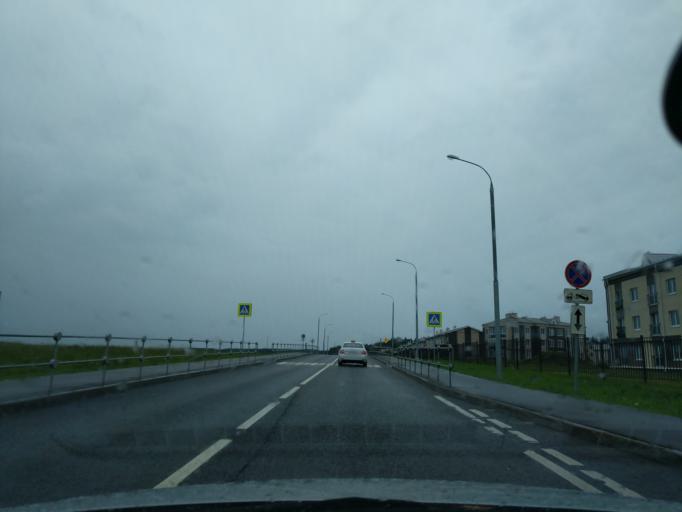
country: RU
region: Moskovskaya
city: Selyatino
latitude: 55.4965
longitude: 36.9218
